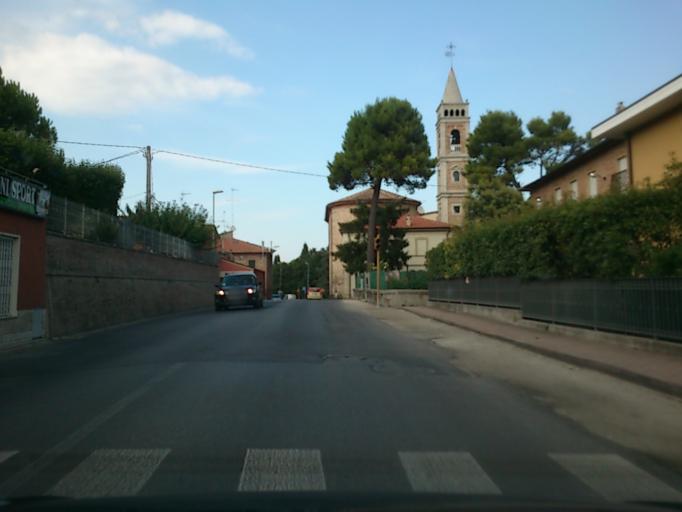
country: IT
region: The Marches
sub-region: Provincia di Pesaro e Urbino
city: Rosciano
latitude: 43.8180
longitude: 12.9910
